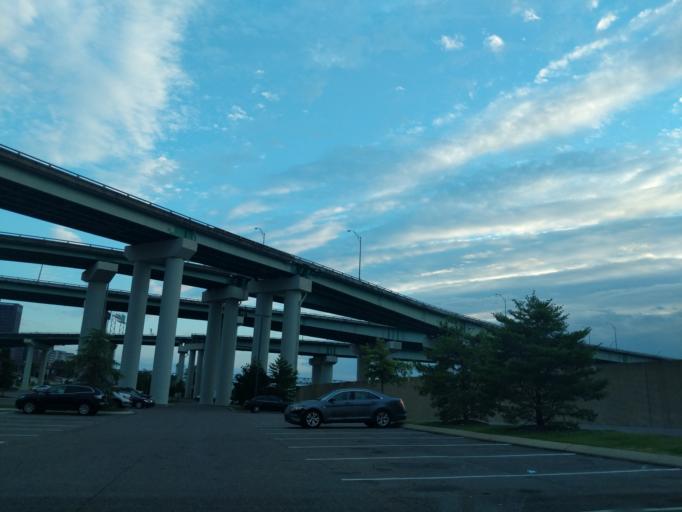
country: US
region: Tennessee
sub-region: Shelby County
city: Memphis
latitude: 35.1545
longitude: -90.0532
